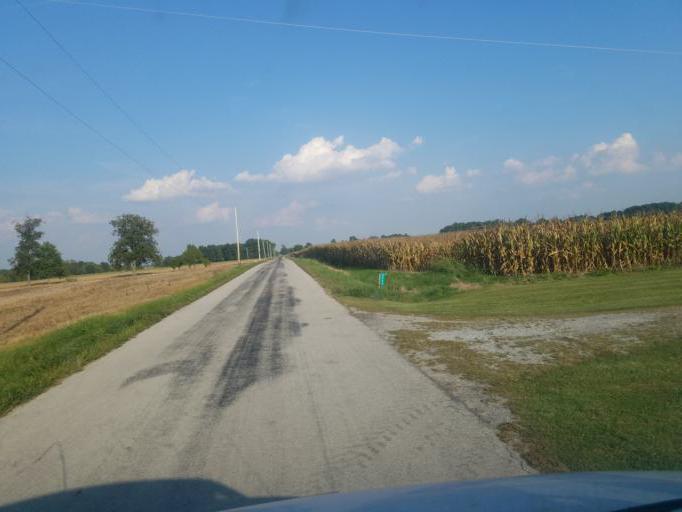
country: US
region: Ohio
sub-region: Wyandot County
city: Upper Sandusky
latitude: 40.9061
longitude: -83.1942
